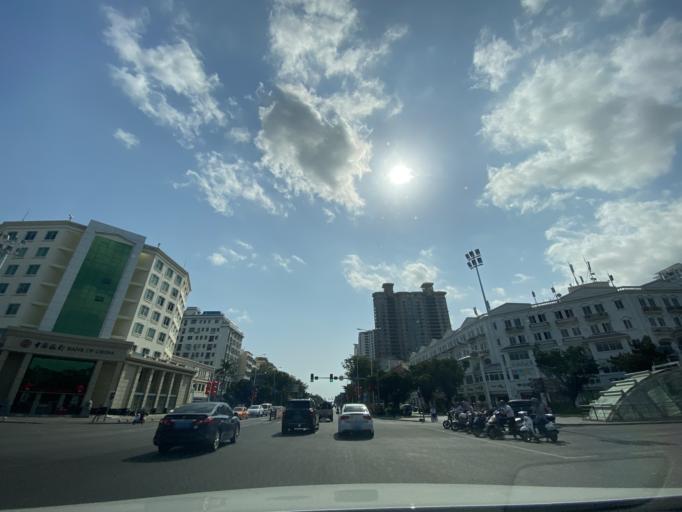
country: CN
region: Hainan
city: Sanya
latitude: 18.2655
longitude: 109.4953
